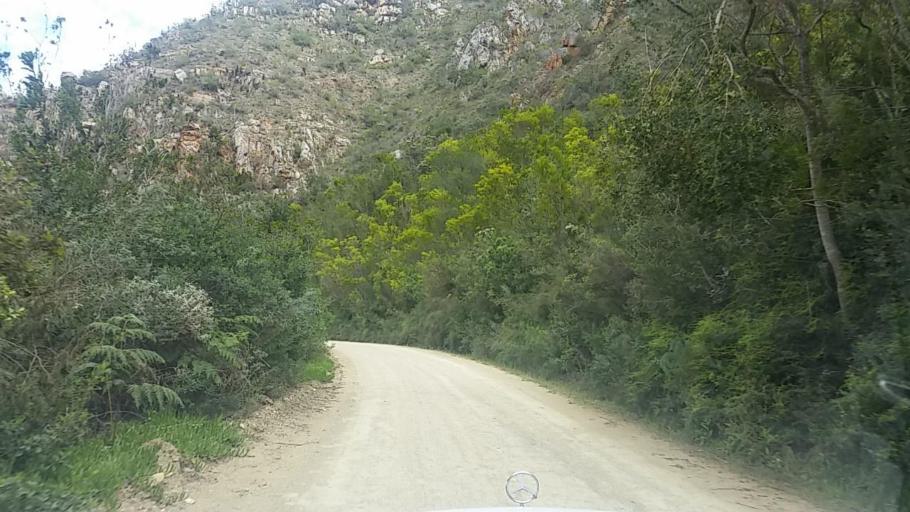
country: ZA
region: Western Cape
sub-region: Eden District Municipality
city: Knysna
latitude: -33.8057
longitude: 23.1813
